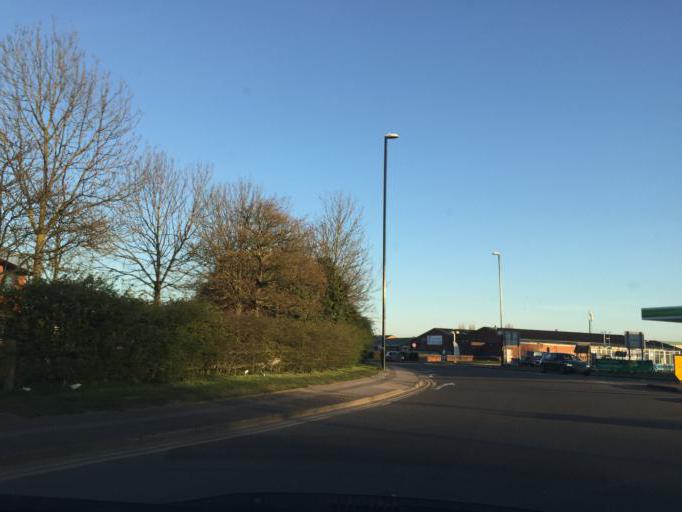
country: GB
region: England
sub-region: Warwickshire
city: Ryton on Dunsmore
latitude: 52.3991
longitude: -1.4413
